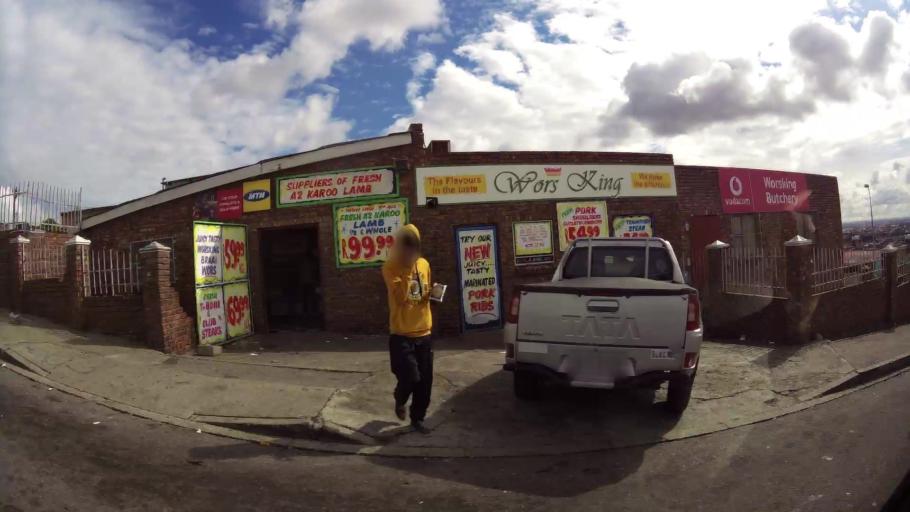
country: ZA
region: Eastern Cape
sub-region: Nelson Mandela Bay Metropolitan Municipality
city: Port Elizabeth
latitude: -33.9308
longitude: 25.5615
